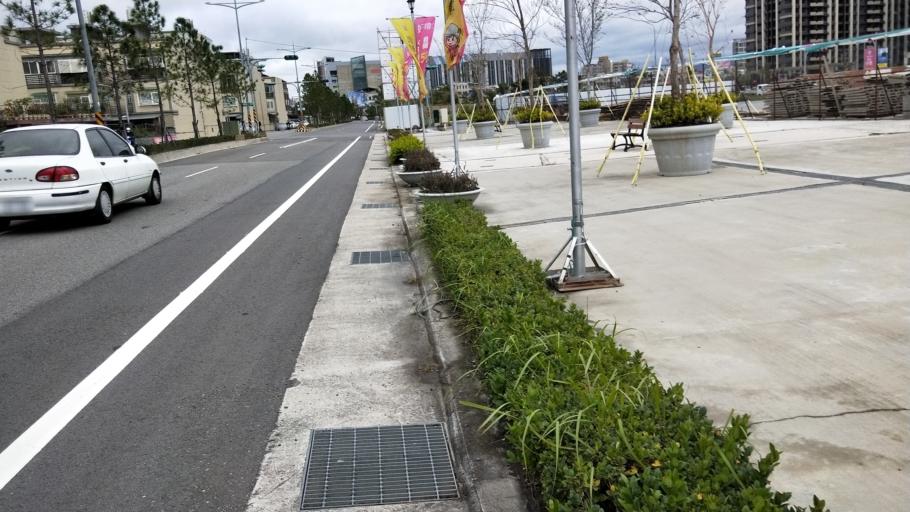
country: TW
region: Taiwan
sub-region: Hsinchu
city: Hsinchu
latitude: 24.6887
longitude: 120.8970
